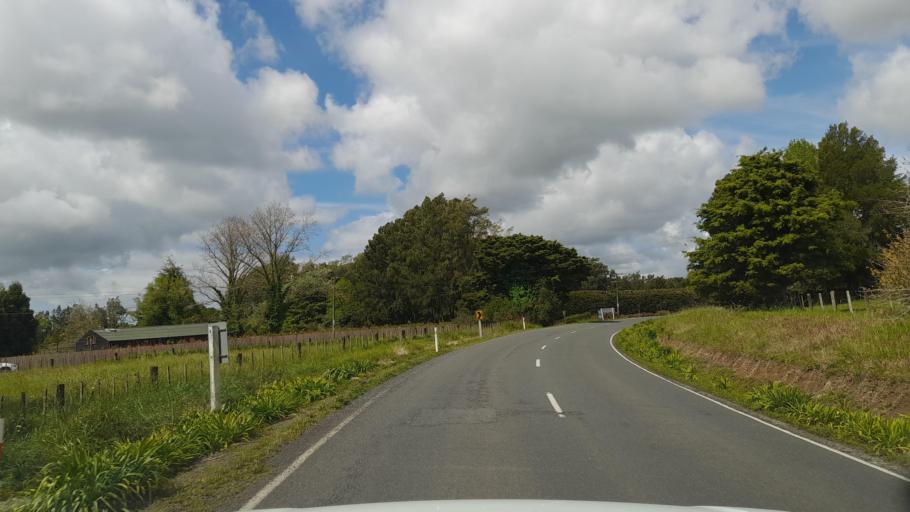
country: NZ
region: Northland
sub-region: Whangarei
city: Maungatapere
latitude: -35.6562
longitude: 174.1731
